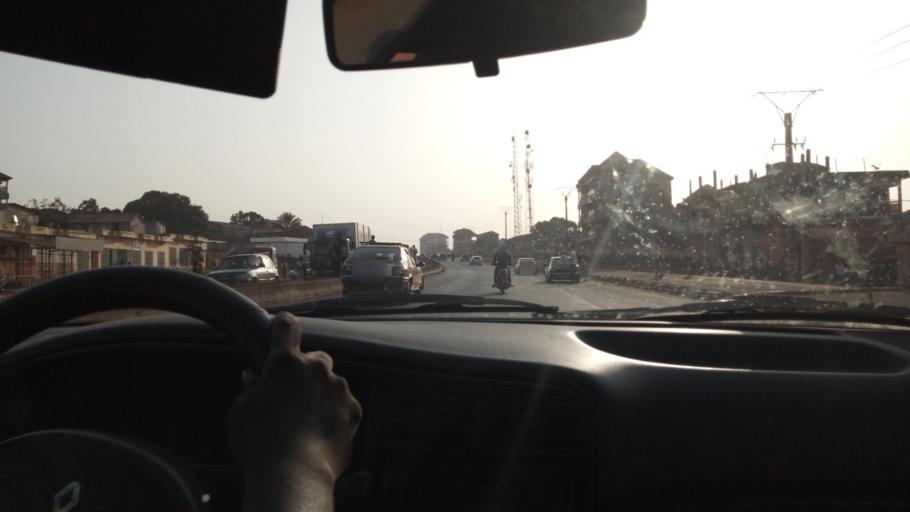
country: GN
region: Kindia
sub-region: Prefecture de Dubreka
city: Dubreka
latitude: 9.6792
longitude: -13.5393
